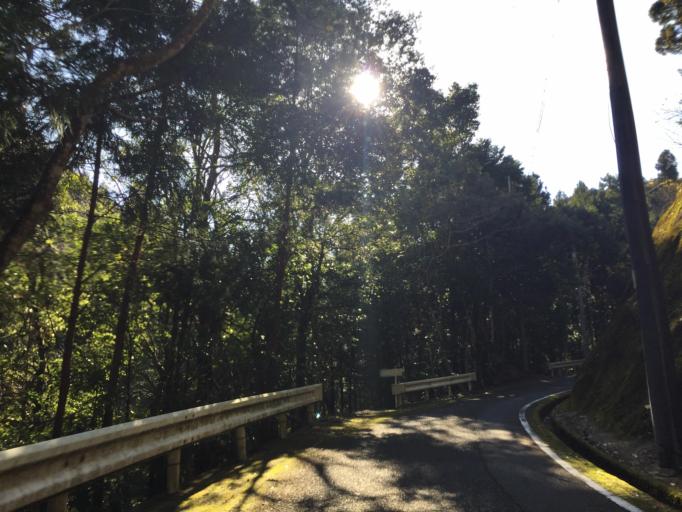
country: JP
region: Wakayama
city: Iwade
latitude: 34.1430
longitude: 135.4181
